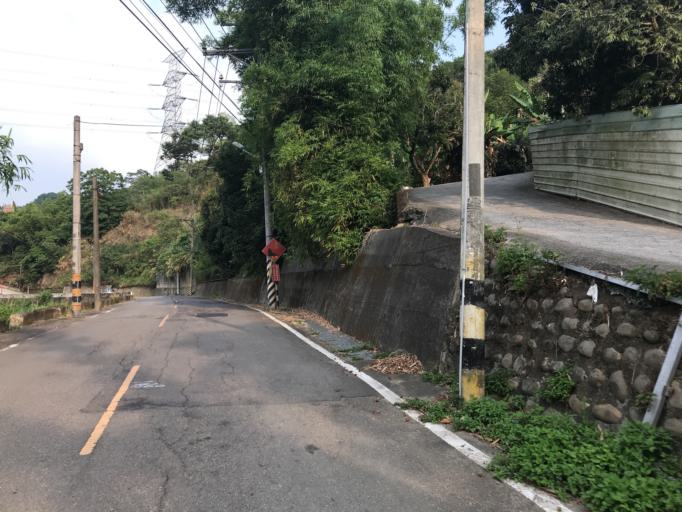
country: TW
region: Taiwan
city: Zhongxing New Village
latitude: 24.0373
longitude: 120.7112
